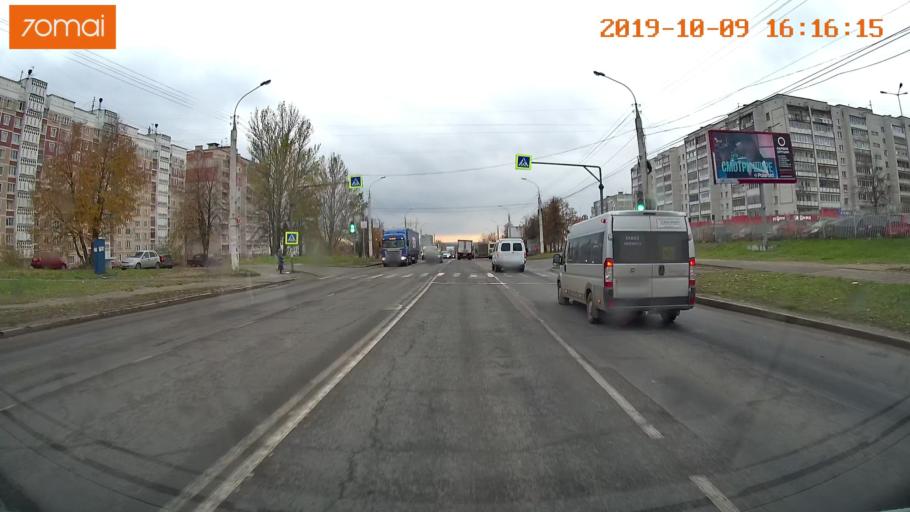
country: RU
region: Kostroma
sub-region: Kostromskoy Rayon
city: Kostroma
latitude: 57.7354
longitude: 40.9095
